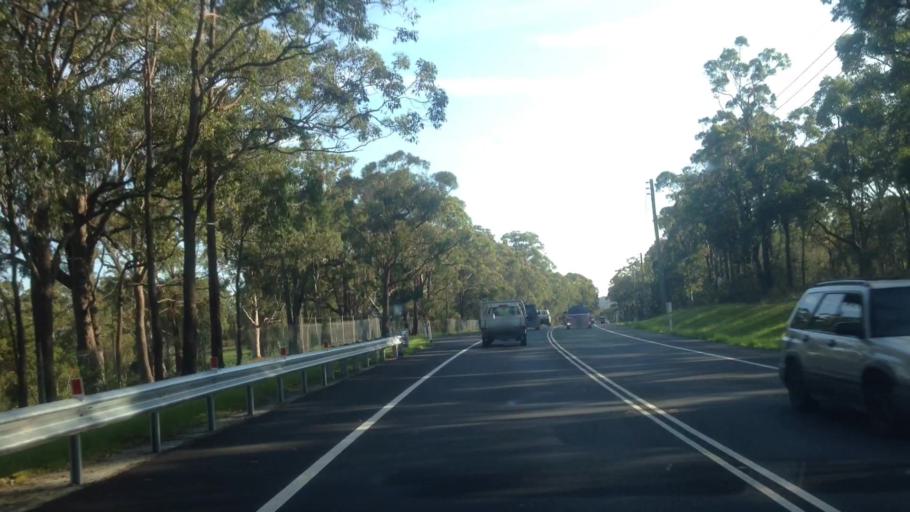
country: AU
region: New South Wales
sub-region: Lake Macquarie Shire
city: Dora Creek
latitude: -33.1200
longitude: 151.4777
